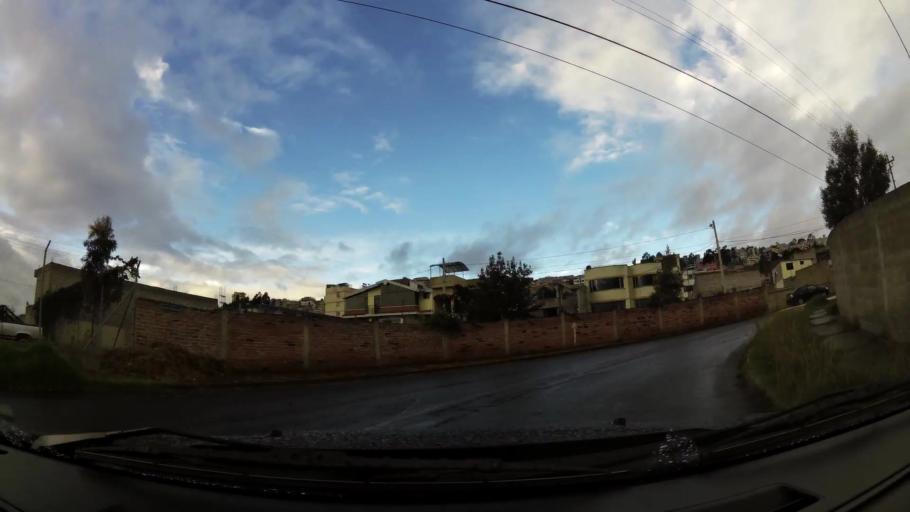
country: EC
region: Pichincha
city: Quito
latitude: -0.1048
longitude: -78.4880
